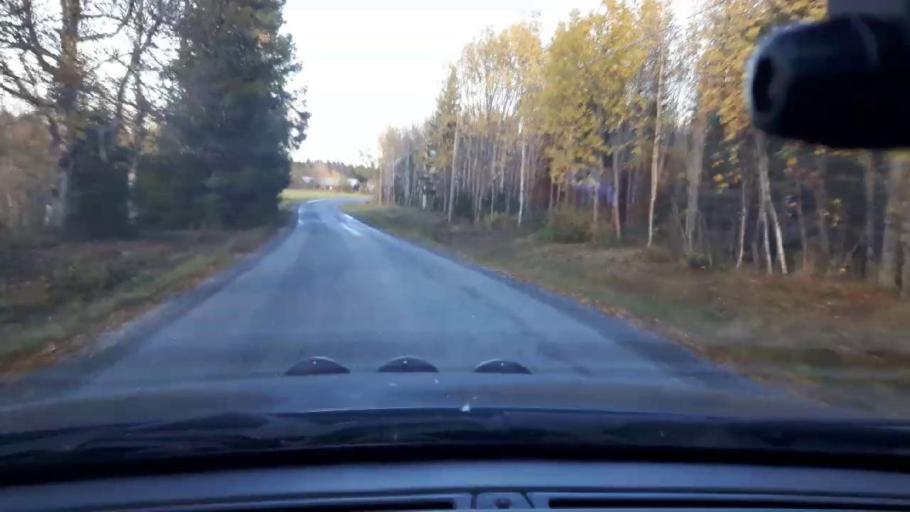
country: SE
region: Jaemtland
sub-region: Bergs Kommun
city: Hoverberg
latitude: 63.0624
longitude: 14.2584
